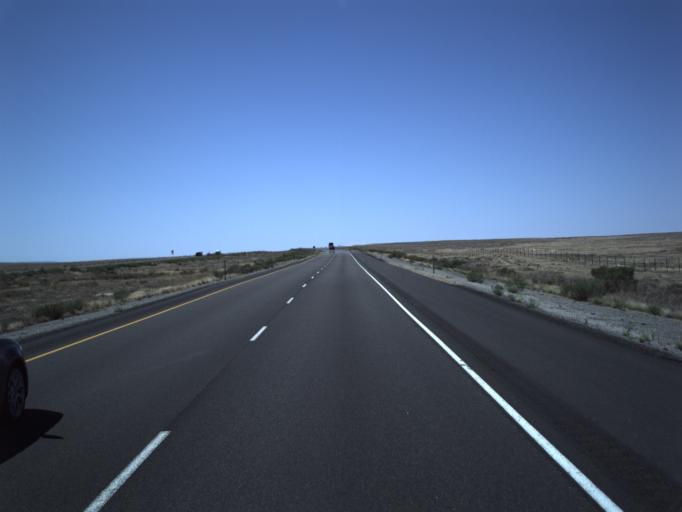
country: US
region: Colorado
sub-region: Mesa County
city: Loma
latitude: 39.0682
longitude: -109.2435
